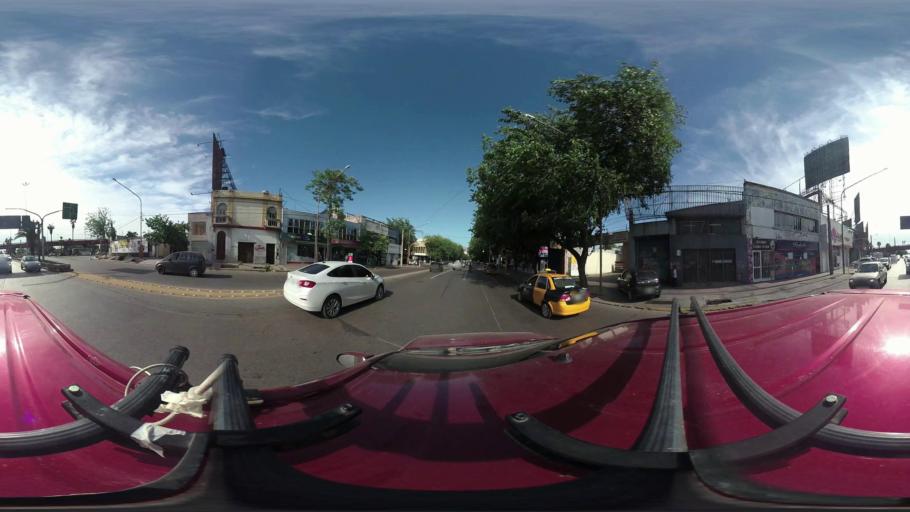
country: AR
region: Mendoza
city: Mendoza
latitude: -32.8961
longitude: -68.8337
